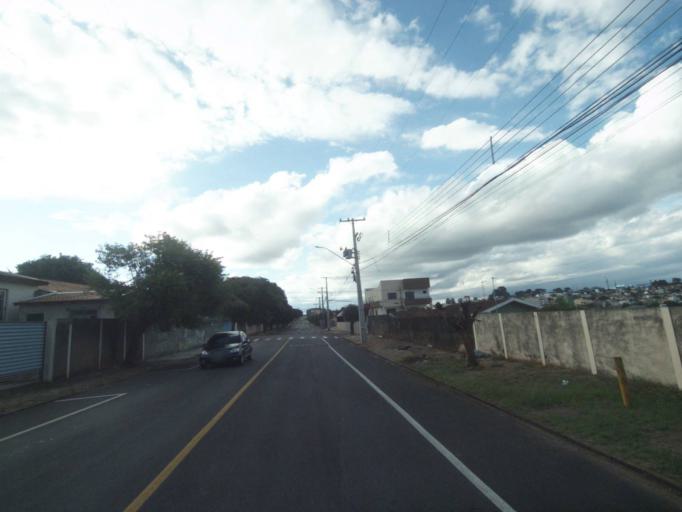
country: BR
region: Parana
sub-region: Telemaco Borba
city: Telemaco Borba
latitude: -24.3398
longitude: -50.6204
